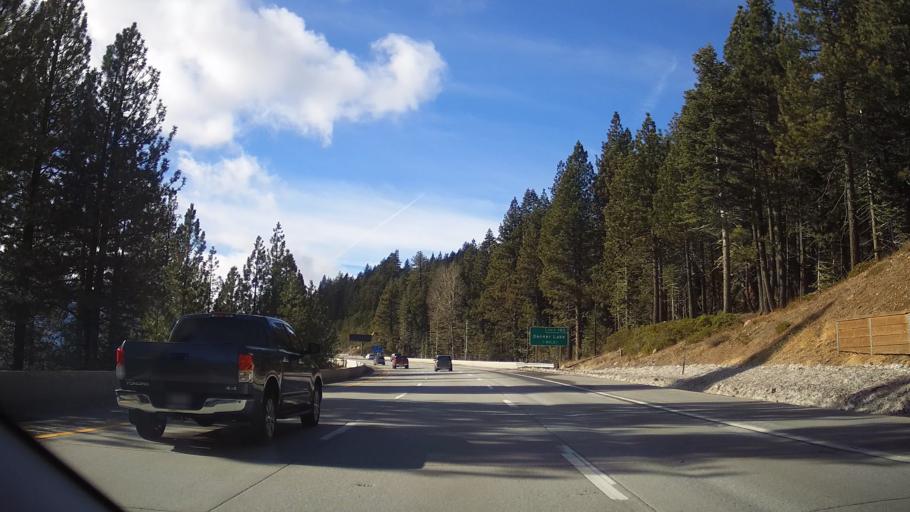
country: US
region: California
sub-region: Nevada County
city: Truckee
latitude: 39.3296
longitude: -120.2661
